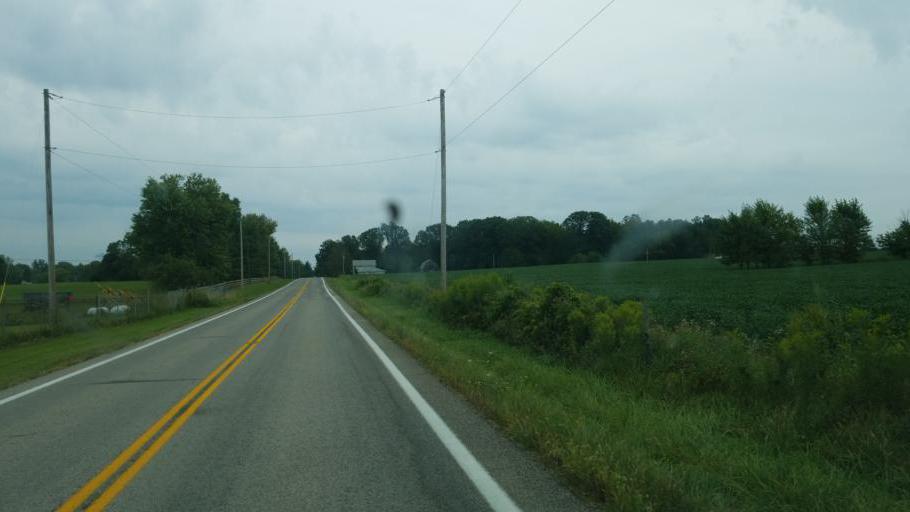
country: US
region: Ohio
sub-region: Morrow County
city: Mount Gilead
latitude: 40.6167
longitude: -82.7660
